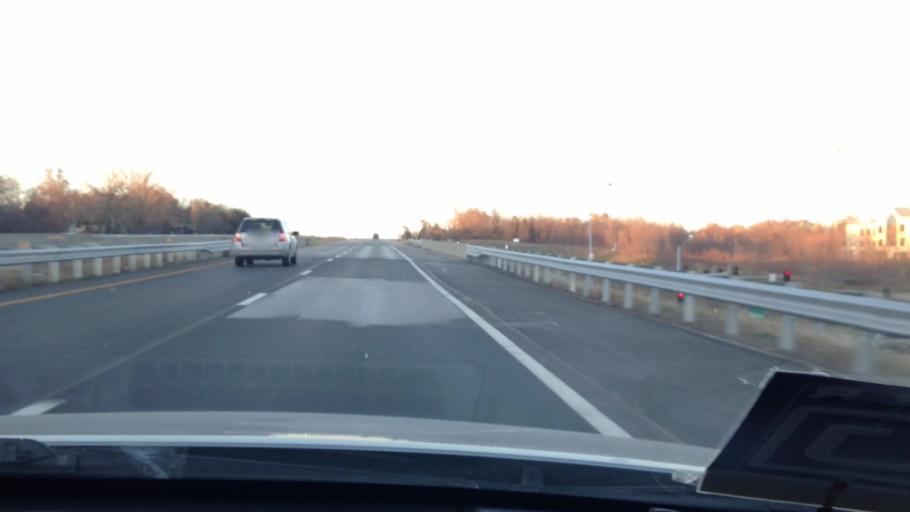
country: US
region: Missouri
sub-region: Clay County
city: Gladstone
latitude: 39.2168
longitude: -94.5893
